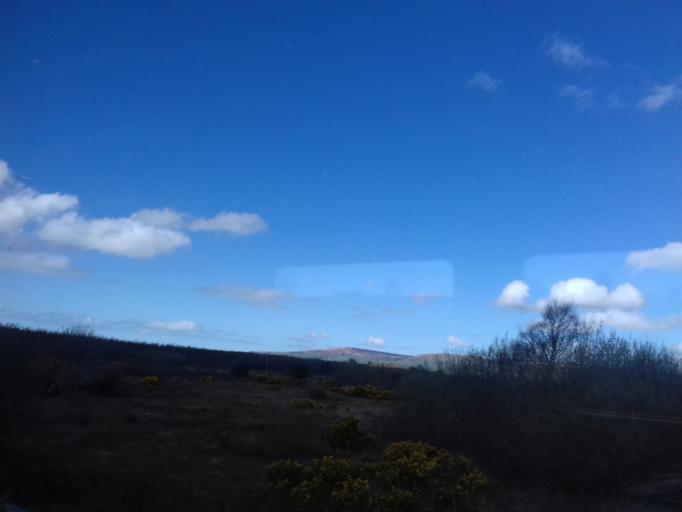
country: IE
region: Munster
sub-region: Ciarrai
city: Tralee
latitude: 52.2374
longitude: -9.5976
